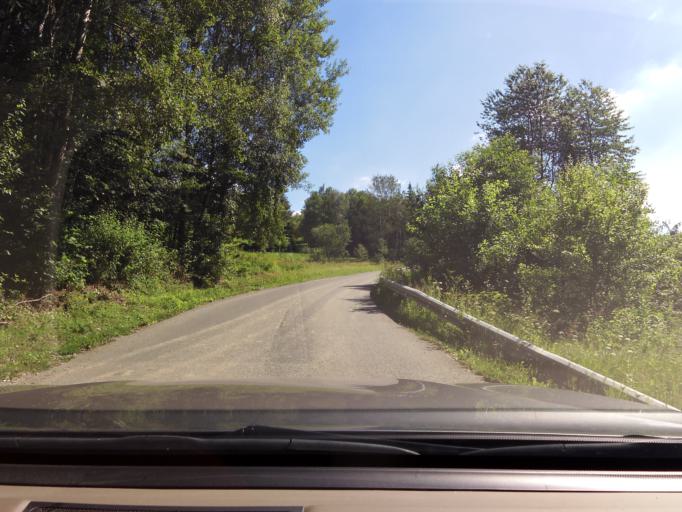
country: PL
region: Silesian Voivodeship
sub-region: Powiat cieszynski
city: Jaworzynka
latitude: 49.4670
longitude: 18.9068
